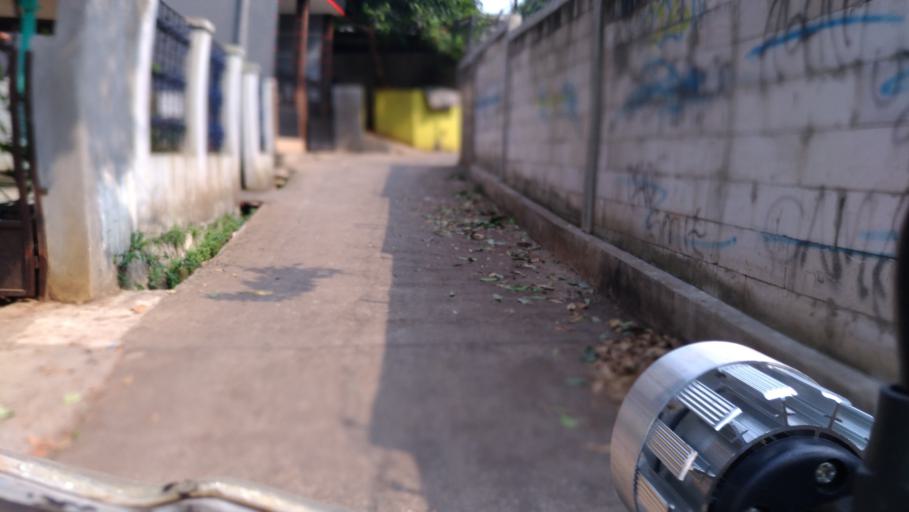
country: ID
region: West Java
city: Depok
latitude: -6.3703
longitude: 106.8764
